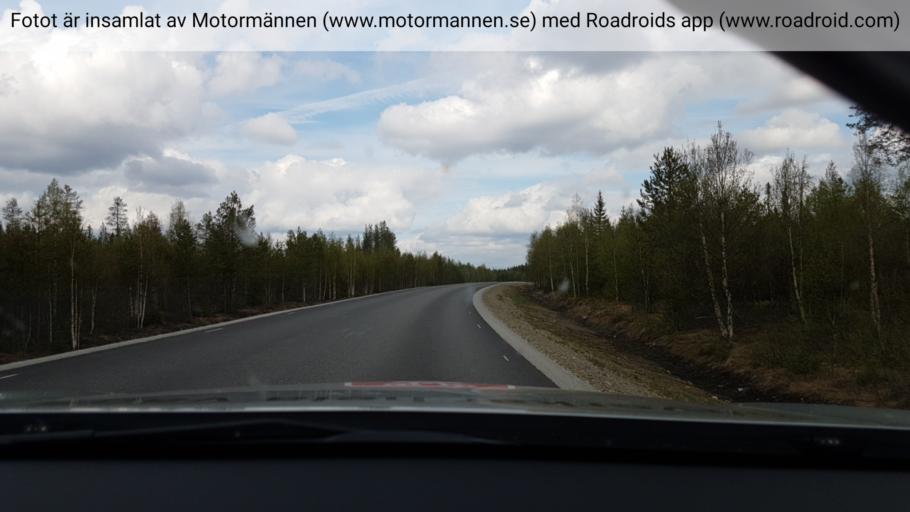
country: SE
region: Vaesterbotten
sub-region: Lycksele Kommun
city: Lycksele
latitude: 64.0315
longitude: 18.4426
